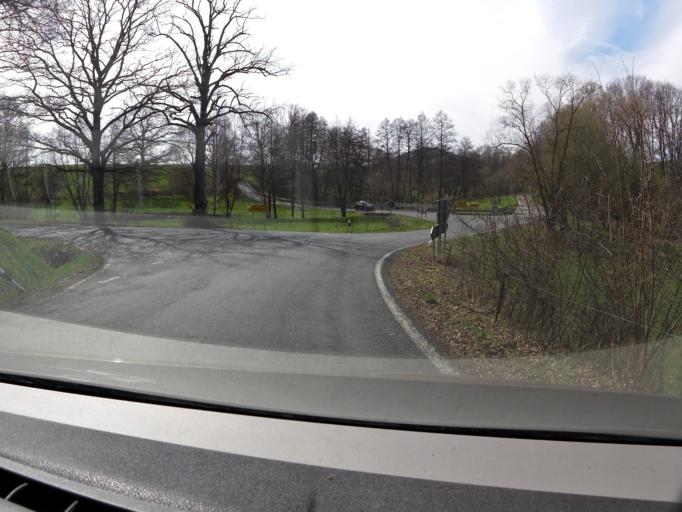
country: DE
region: Thuringia
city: Wolferbutt
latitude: 50.7601
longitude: 10.0600
